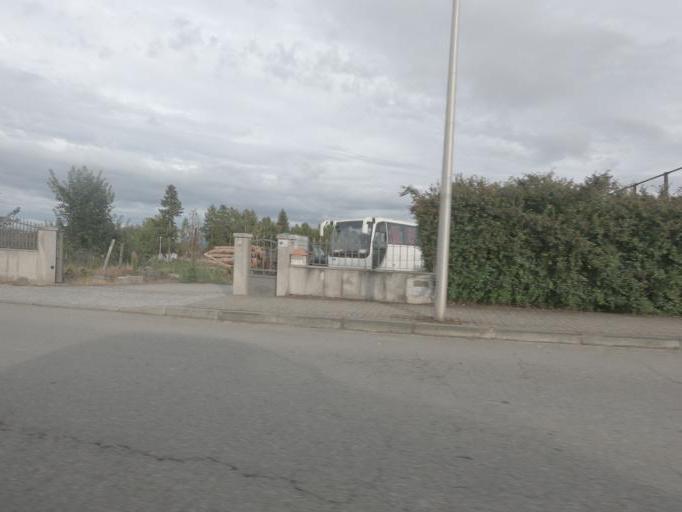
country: PT
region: Vila Real
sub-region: Sabrosa
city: Sabrosa
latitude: 41.2630
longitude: -7.5826
